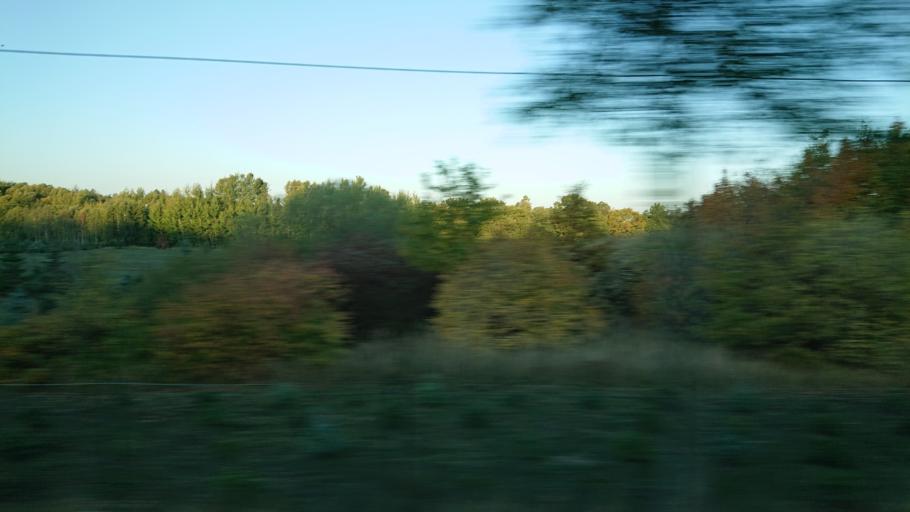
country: DE
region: Mecklenburg-Vorpommern
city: Trollenhagen
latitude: 53.6375
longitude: 13.2685
